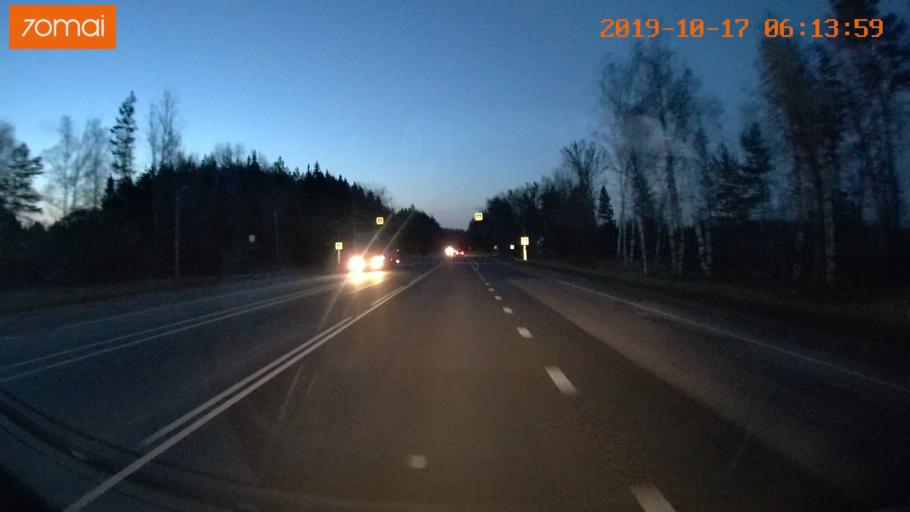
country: RU
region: Ivanovo
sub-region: Gorod Ivanovo
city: Ivanovo
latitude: 56.8914
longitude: 40.9399
